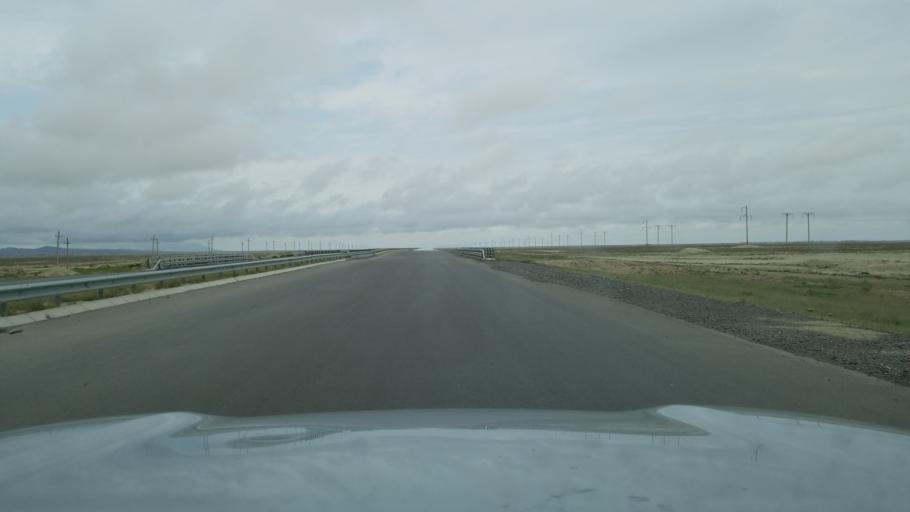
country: TM
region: Balkan
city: Serdar
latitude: 39.1105
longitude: 55.9246
